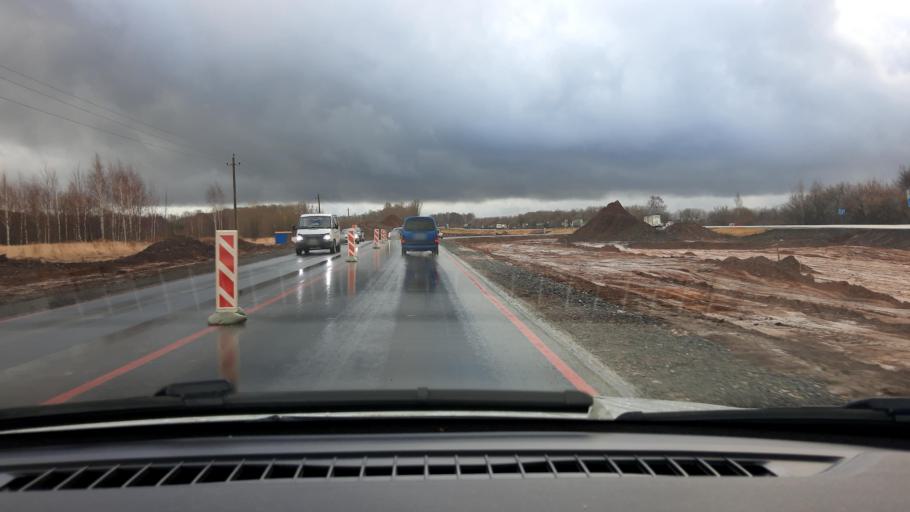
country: RU
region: Nizjnij Novgorod
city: Pamyat' Parizhskoy Kommuny
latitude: 56.0165
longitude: 44.6261
